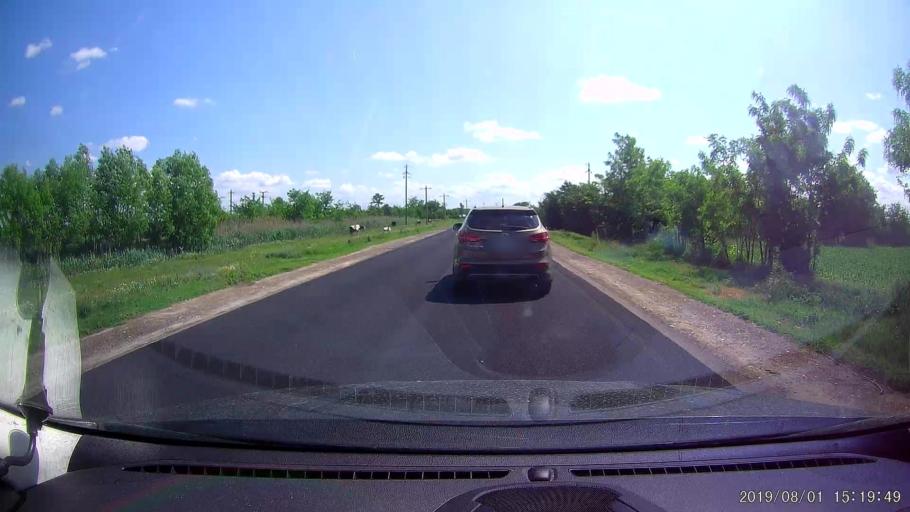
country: RO
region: Braila
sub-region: Comuna Unirea
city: Unirea
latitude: 45.0852
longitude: 27.8111
